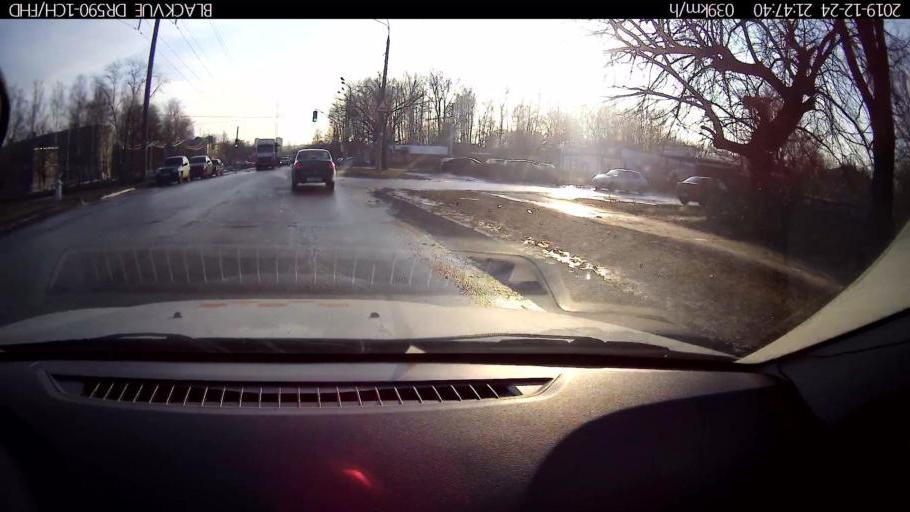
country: RU
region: Nizjnij Novgorod
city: Gorbatovka
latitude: 56.2293
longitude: 43.8418
